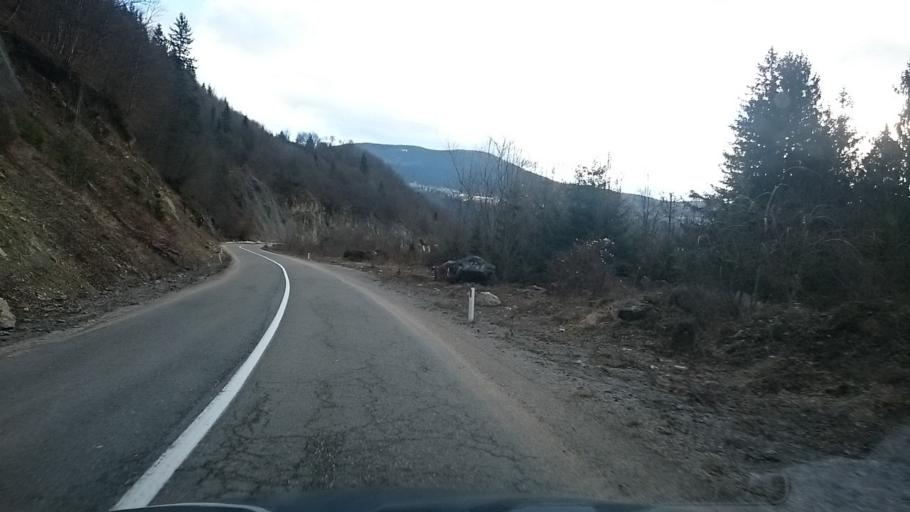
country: BA
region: Republika Srpska
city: Skender Vakuf
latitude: 44.4658
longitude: 17.3737
